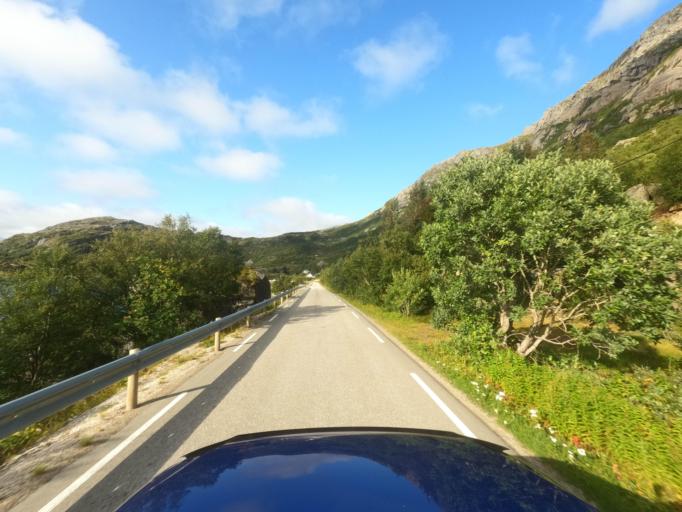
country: NO
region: Nordland
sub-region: Flakstad
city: Ramberg
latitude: 68.0166
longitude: 13.2005
